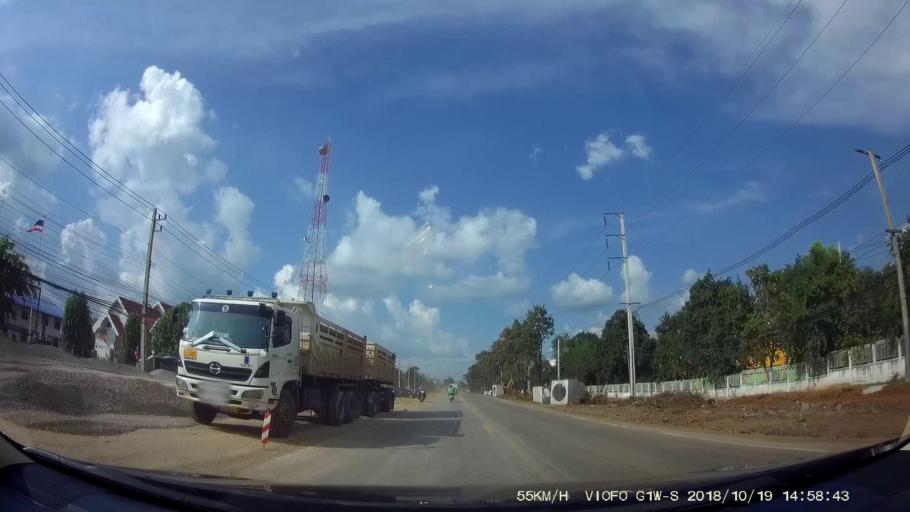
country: TH
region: Chaiyaphum
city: Phu Khiao
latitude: 16.3772
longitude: 102.1293
